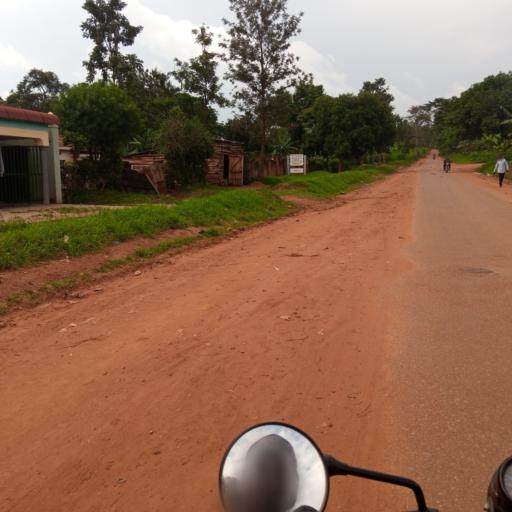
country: UG
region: Eastern Region
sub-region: Mbale District
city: Mbale
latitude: 1.0891
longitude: 34.1847
